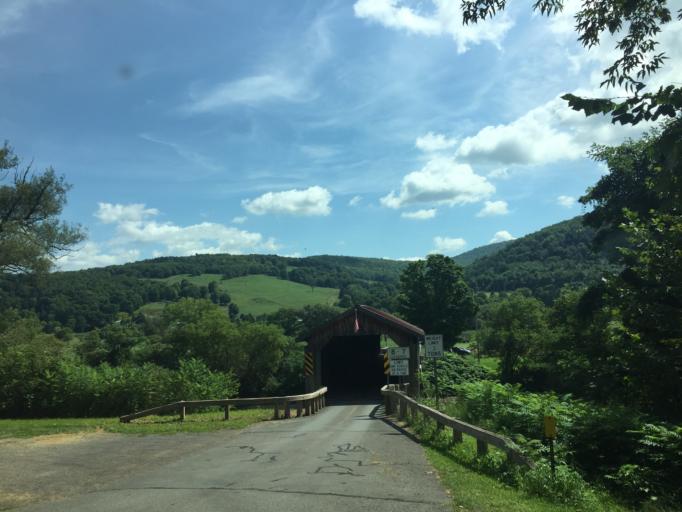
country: US
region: New York
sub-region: Delaware County
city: Delhi
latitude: 42.1958
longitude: -74.9890
